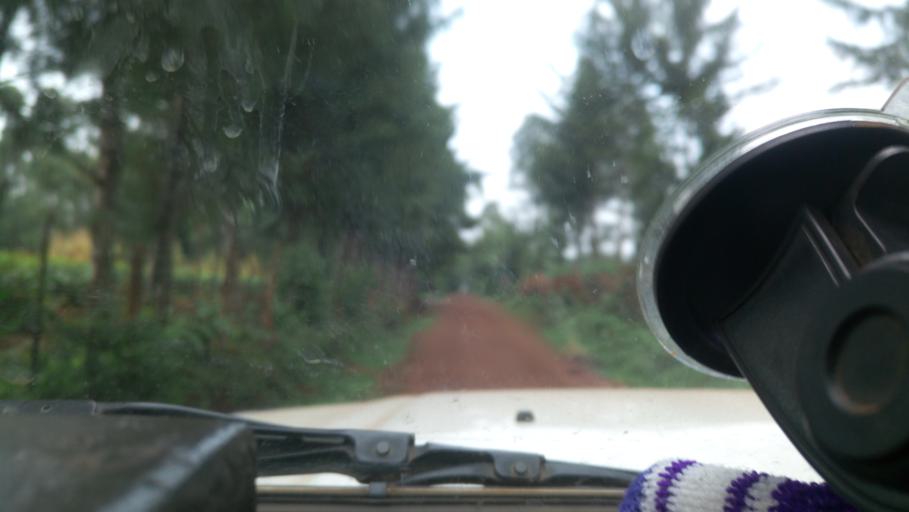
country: KE
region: Kericho
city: Sotik
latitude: -0.6540
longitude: 35.1518
